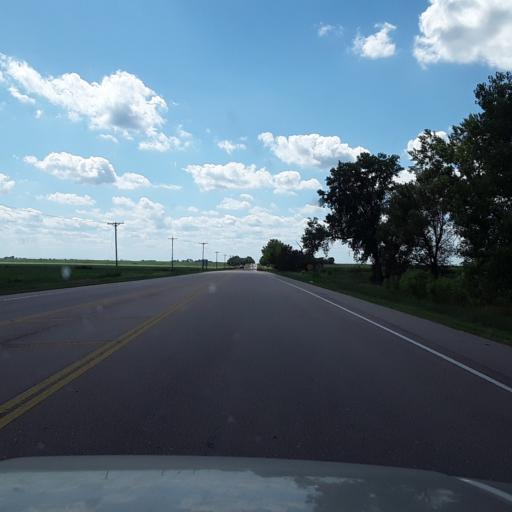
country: US
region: Nebraska
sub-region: Merrick County
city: Central City
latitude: 41.1911
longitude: -98.0039
